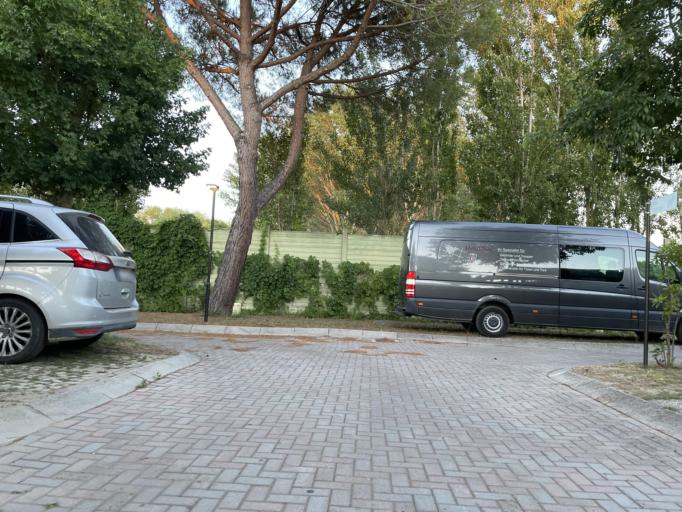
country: IT
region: Emilia-Romagna
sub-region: Provincia di Ferrara
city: San Giuseppe
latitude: 44.7318
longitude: 12.2312
